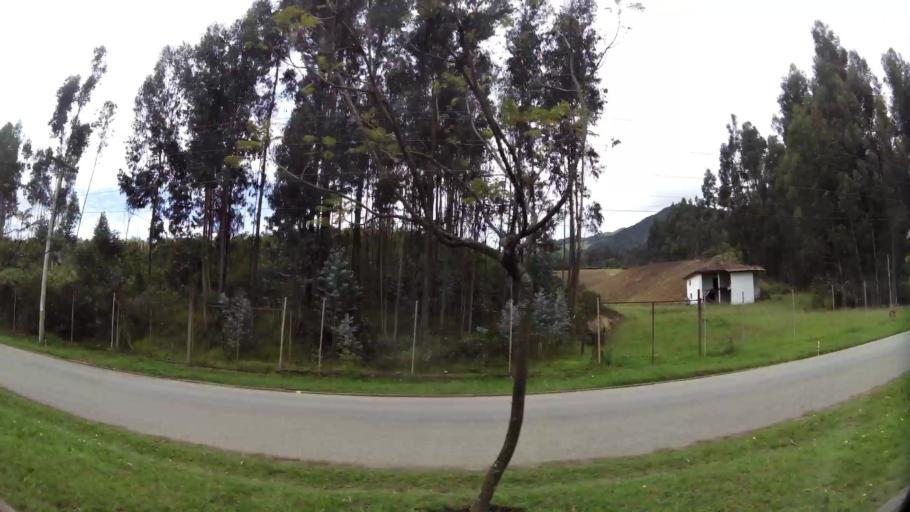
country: EC
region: Azuay
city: Cuenca
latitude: -2.8833
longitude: -79.0696
